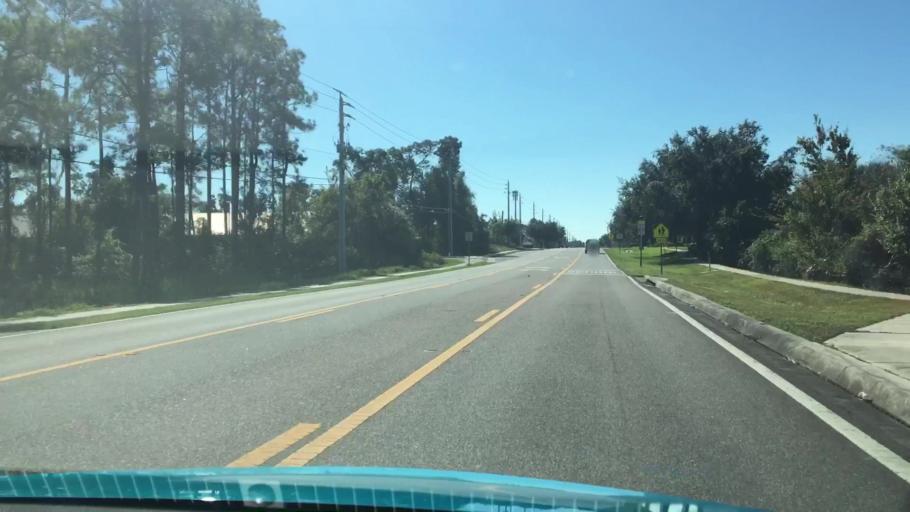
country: US
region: Florida
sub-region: Seminole County
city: Heathrow
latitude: 28.8038
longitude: -81.3630
